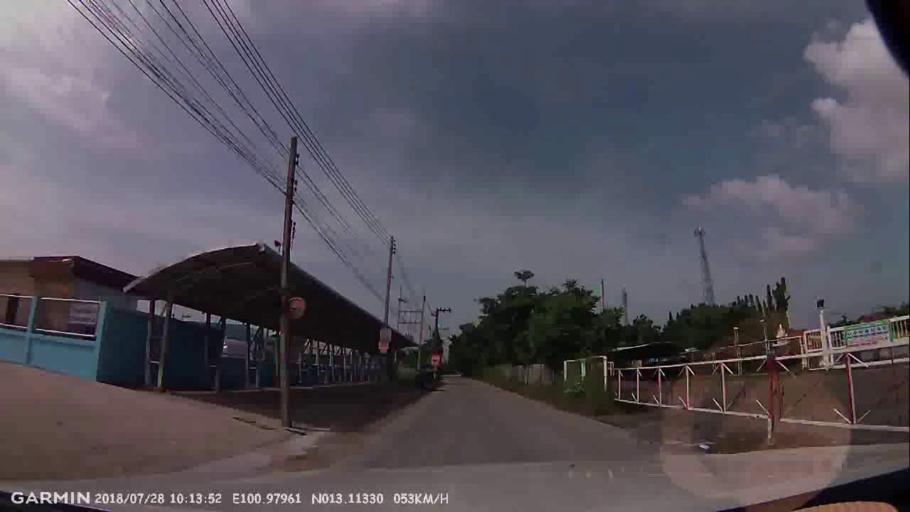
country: TH
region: Chon Buri
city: Ban Talat Bueng
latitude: 13.1132
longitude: 100.9796
